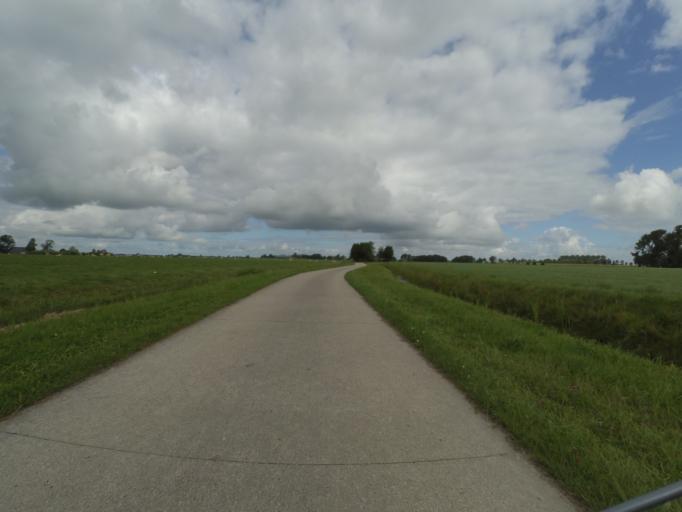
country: NL
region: Friesland
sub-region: Gemeente Kollumerland en Nieuwkruisland
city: Kollum
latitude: 53.2874
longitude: 6.2273
